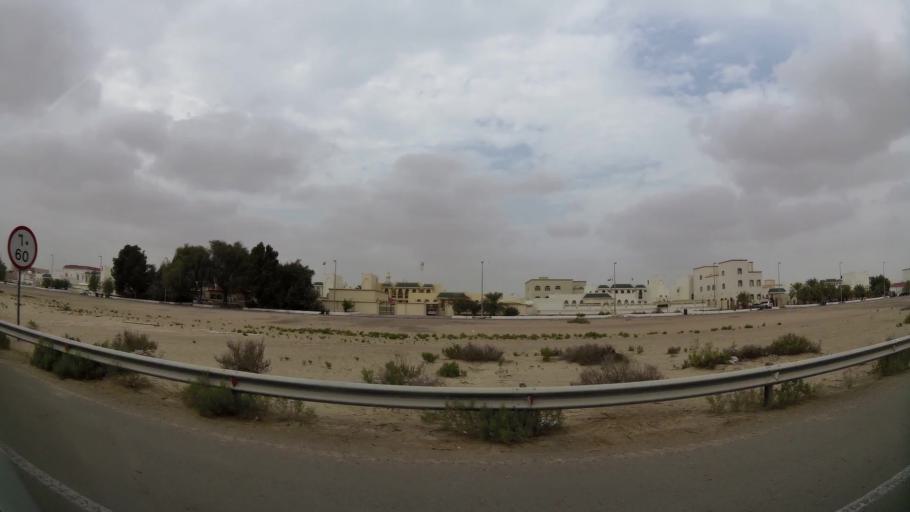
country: AE
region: Abu Dhabi
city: Abu Dhabi
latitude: 24.3419
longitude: 54.6463
